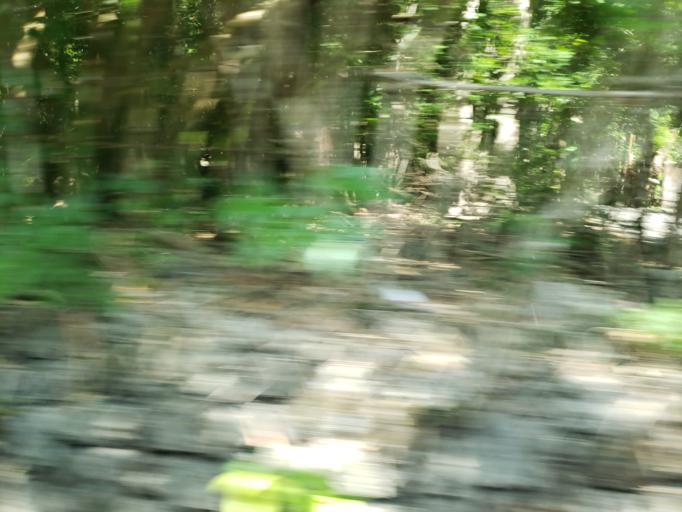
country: ID
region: Bali
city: Pecatu
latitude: -8.8371
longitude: 115.1257
